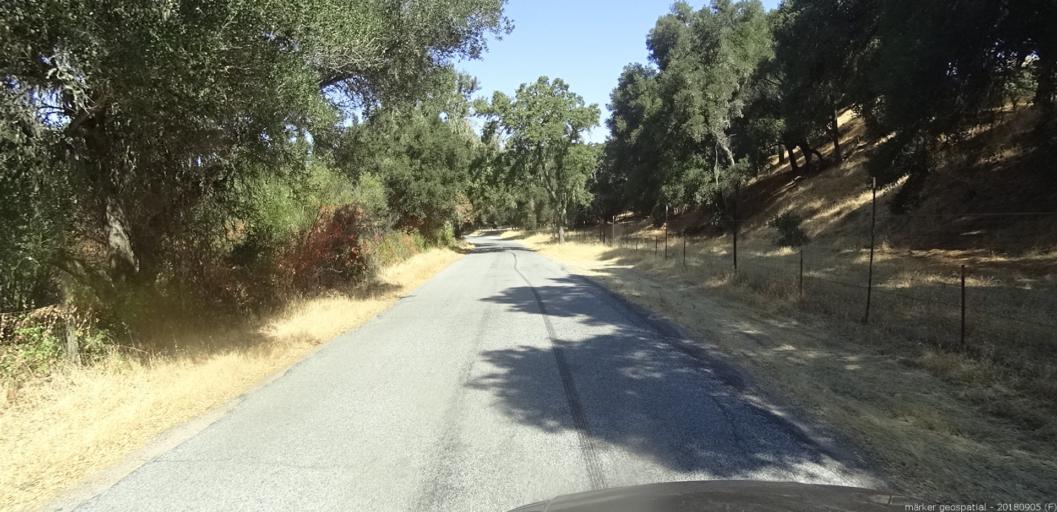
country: US
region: California
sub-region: Monterey County
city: Carmel Valley Village
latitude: 36.3975
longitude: -121.6508
